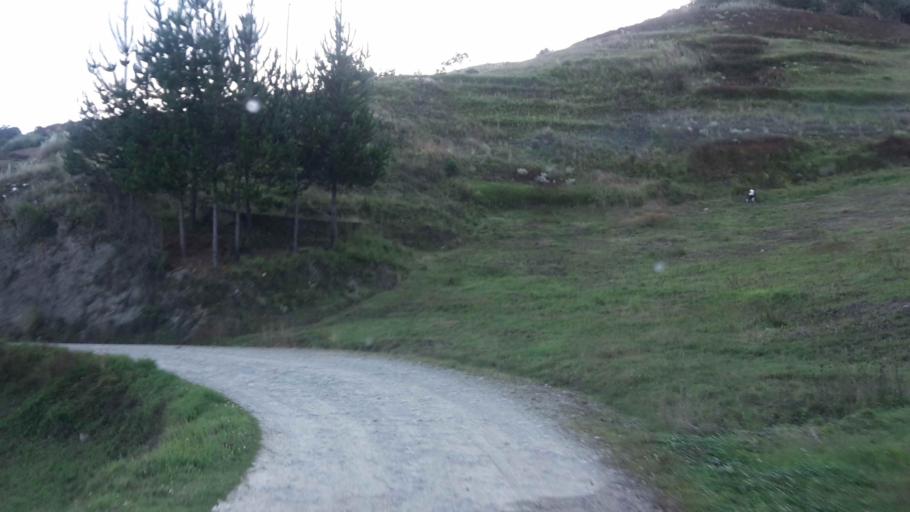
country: BO
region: Cochabamba
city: Colomi
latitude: -17.2725
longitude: -65.9069
